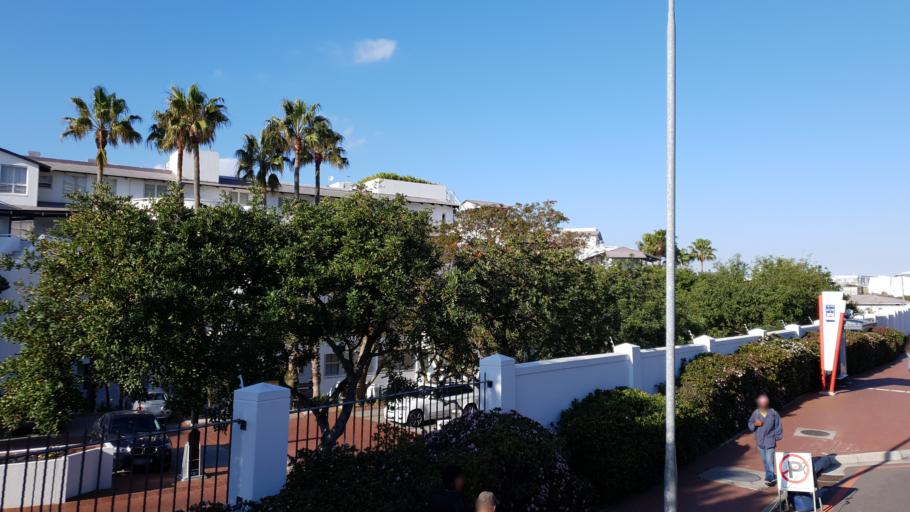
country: ZA
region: Western Cape
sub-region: City of Cape Town
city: Cape Town
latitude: -33.9011
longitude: 18.4127
